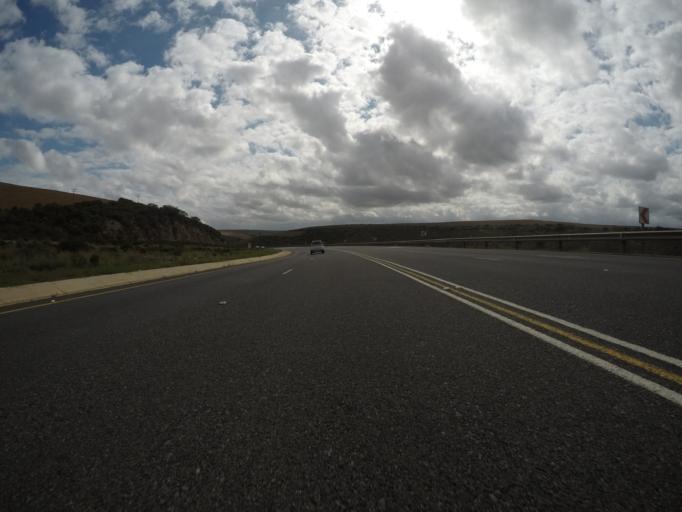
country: ZA
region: Western Cape
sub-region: Eden District Municipality
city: Riversdale
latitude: -34.1463
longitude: 21.2880
